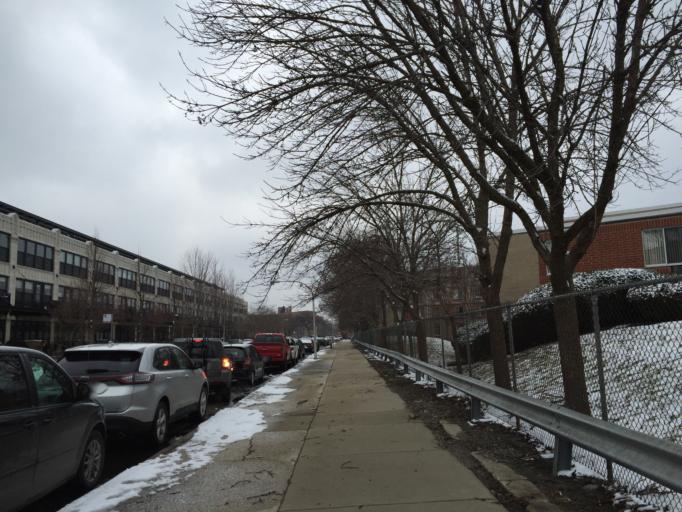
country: US
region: Illinois
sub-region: Cook County
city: Chicago
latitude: 41.8625
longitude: -87.6545
